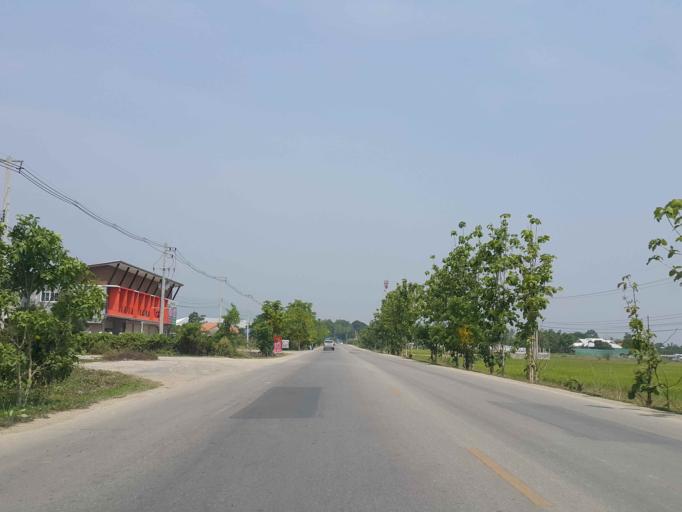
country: TH
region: Chiang Mai
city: San Sai
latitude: 18.8630
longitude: 98.9897
